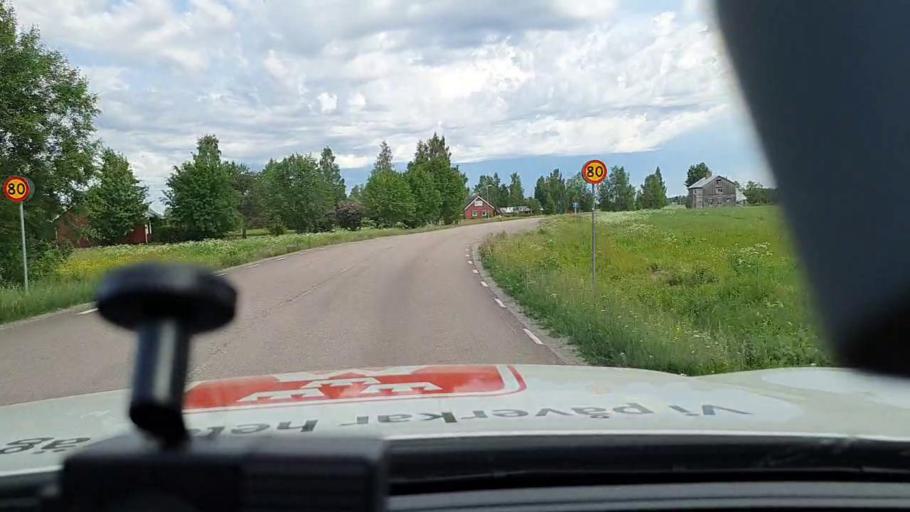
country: SE
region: Norrbotten
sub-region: Bodens Kommun
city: Saevast
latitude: 65.6862
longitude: 21.7854
